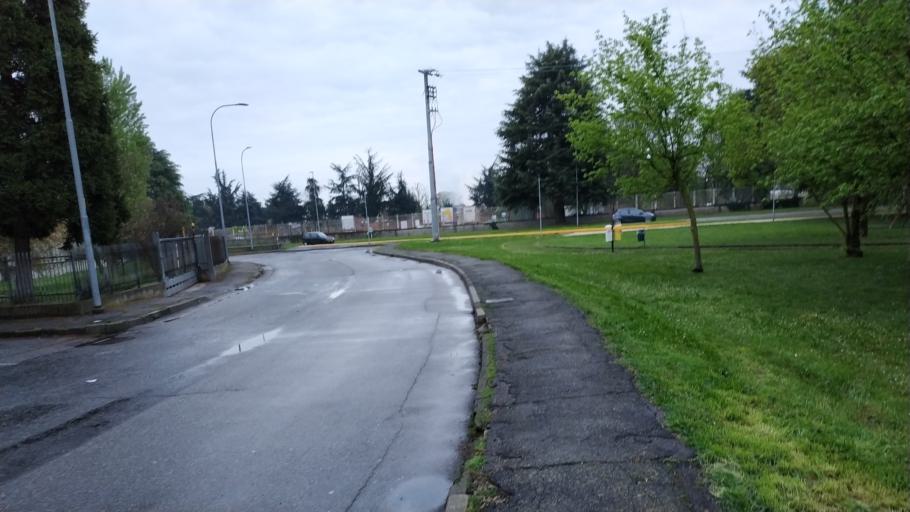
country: IT
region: Lombardy
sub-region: Citta metropolitana di Milano
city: Pregnana Milanese
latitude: 45.5252
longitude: 9.0269
